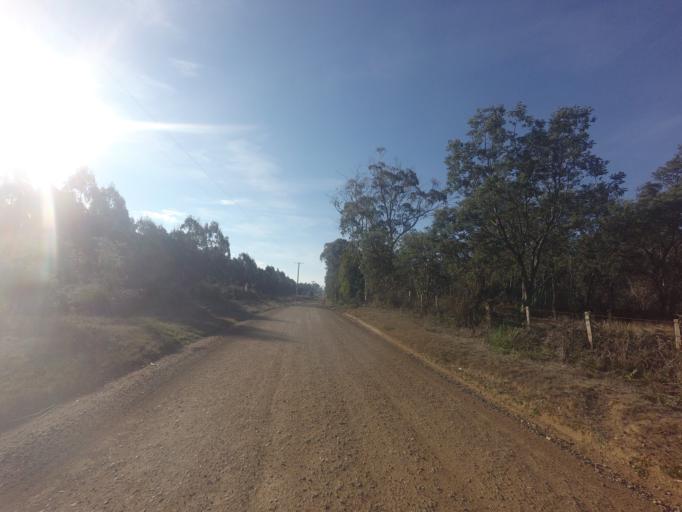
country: AU
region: Tasmania
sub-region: Brighton
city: Bridgewater
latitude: -42.4453
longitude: 147.3857
